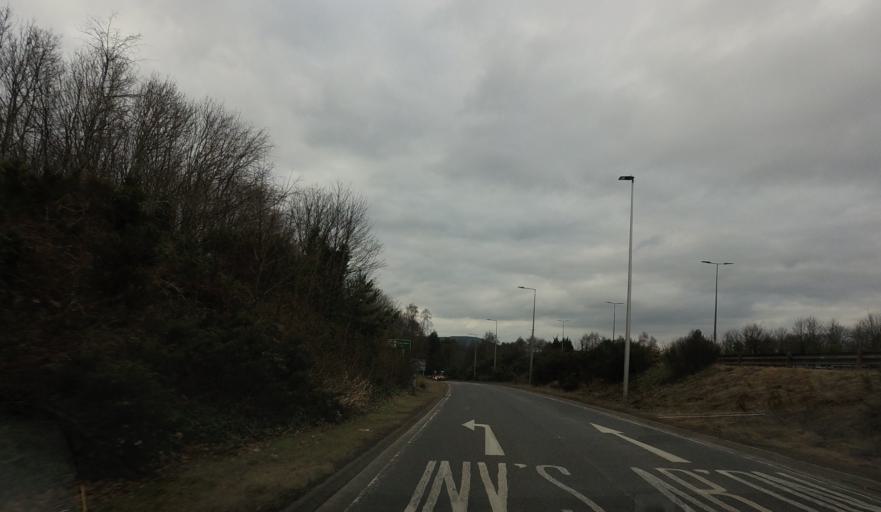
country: GB
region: Scotland
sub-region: Highland
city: Inverness
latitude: 57.4801
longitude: -4.1904
